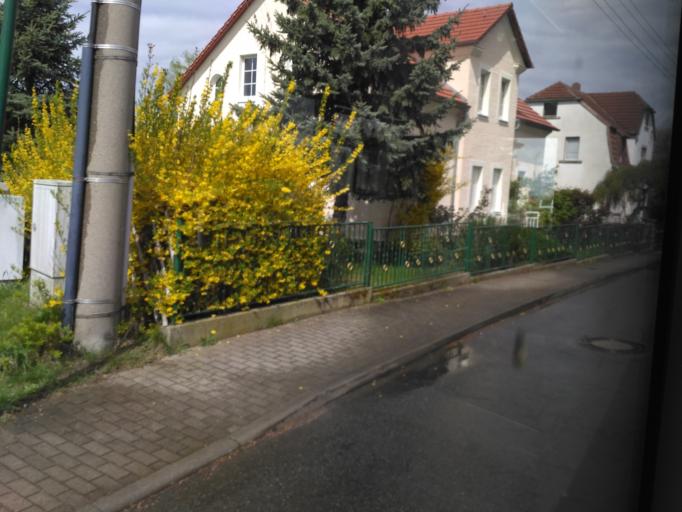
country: DE
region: Saxony
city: Coswig
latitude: 51.0896
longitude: 13.5916
